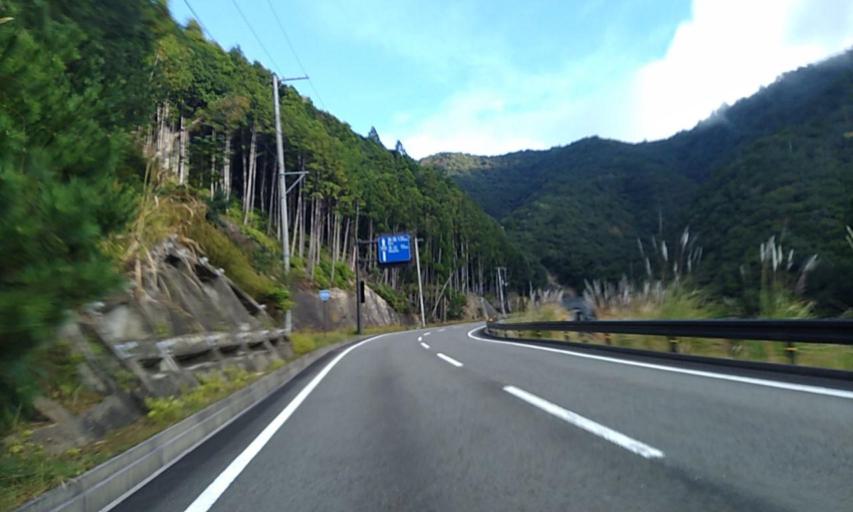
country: JP
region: Wakayama
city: Shingu
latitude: 33.8779
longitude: 135.8761
